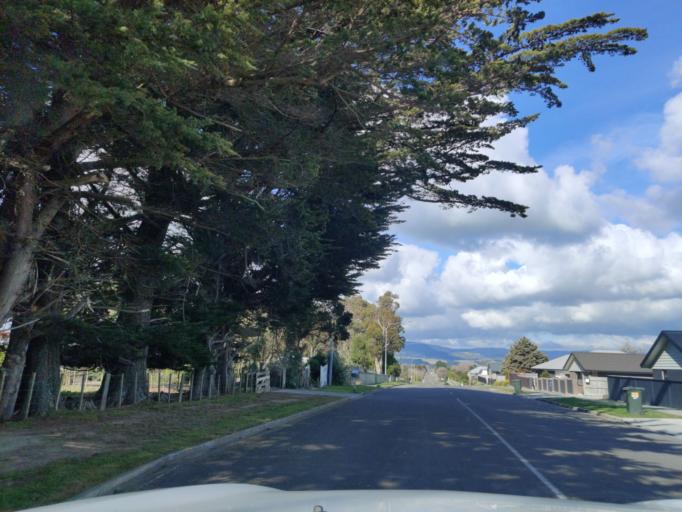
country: NZ
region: Manawatu-Wanganui
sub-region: Palmerston North City
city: Palmerston North
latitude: -40.3206
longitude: 175.6583
